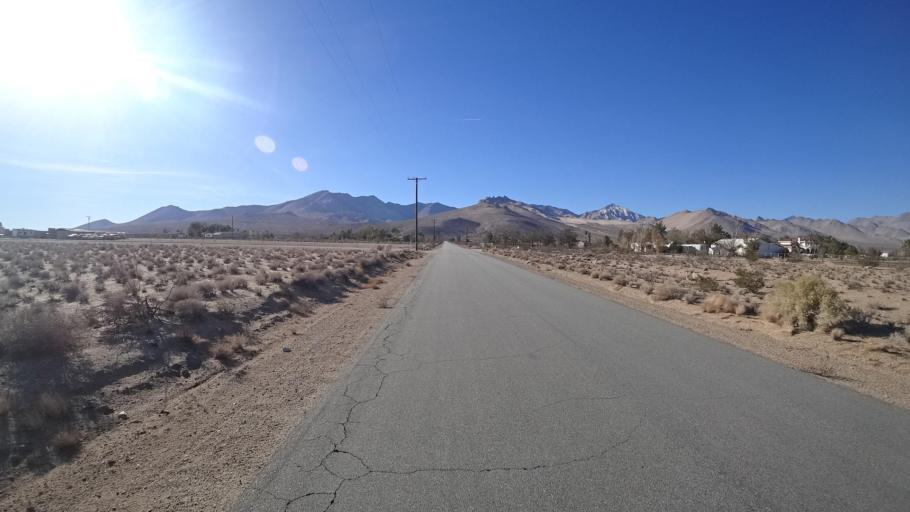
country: US
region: California
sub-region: Kern County
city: Inyokern
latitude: 35.6812
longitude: -117.8499
